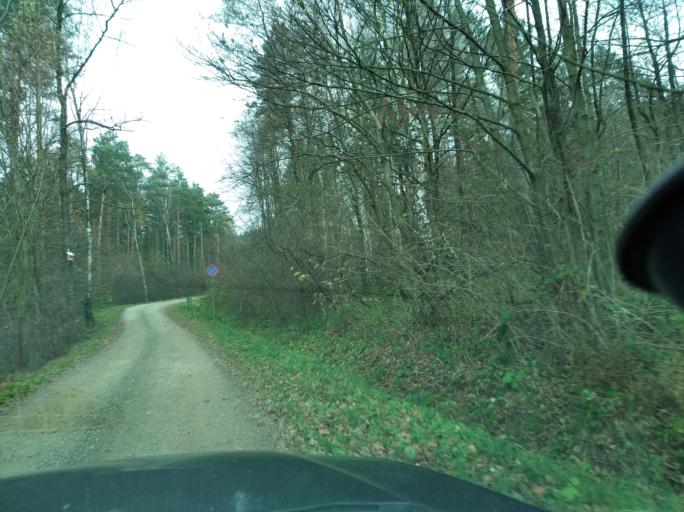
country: PL
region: Subcarpathian Voivodeship
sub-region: Powiat strzyzowski
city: Wysoka Strzyzowska
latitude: 49.7887
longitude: 21.7661
